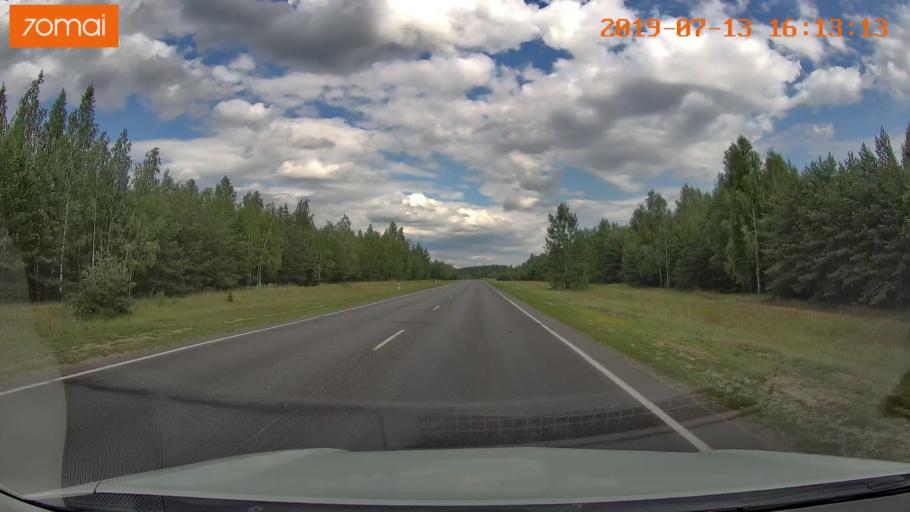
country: BY
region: Mogilev
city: Babruysk
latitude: 53.1638
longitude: 29.2984
